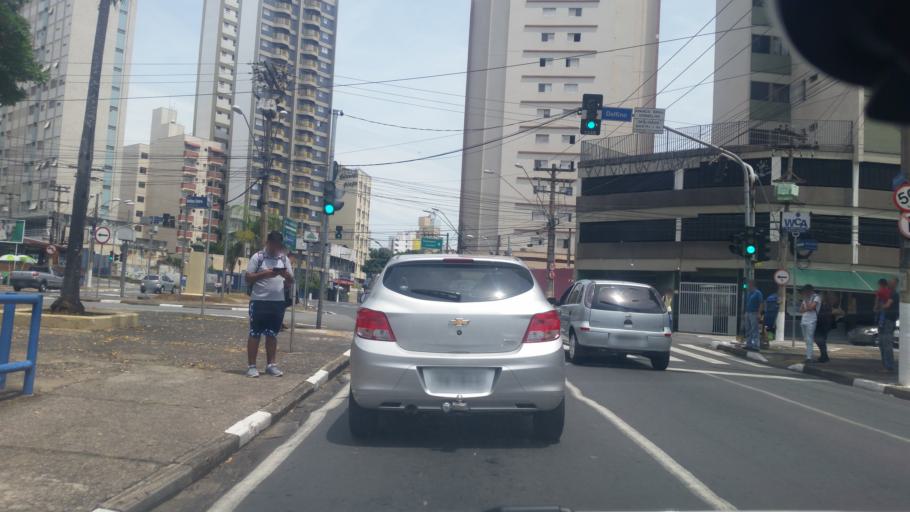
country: BR
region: Sao Paulo
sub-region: Campinas
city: Campinas
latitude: -22.9004
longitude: -47.0634
